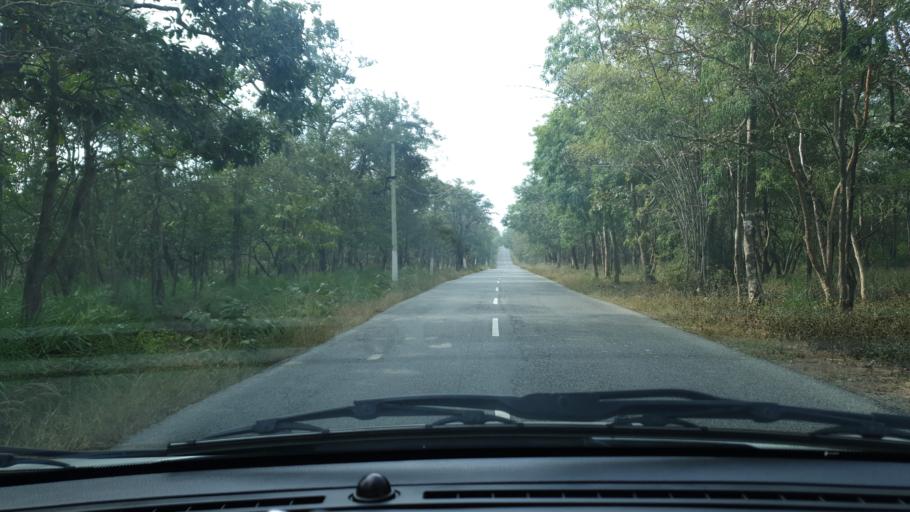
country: IN
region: Andhra Pradesh
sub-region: Kurnool
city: Srisailam
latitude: 16.2906
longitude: 78.7301
